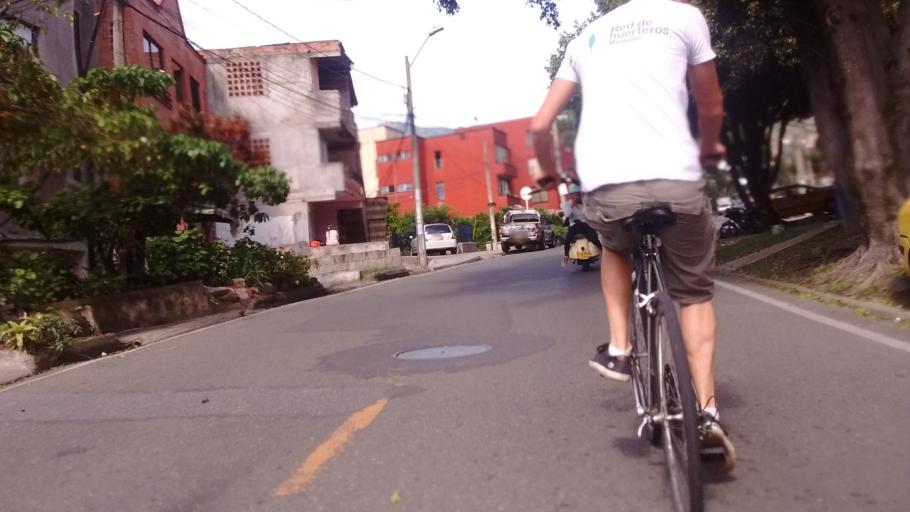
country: CO
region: Antioquia
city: Medellin
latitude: 6.2546
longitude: -75.6179
